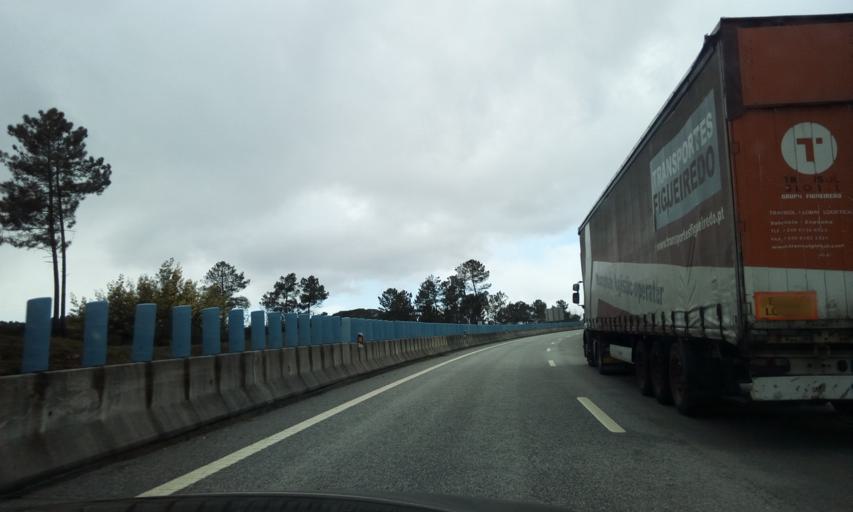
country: PT
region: Viseu
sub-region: Viseu
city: Rio de Loba
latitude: 40.6445
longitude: -7.8599
